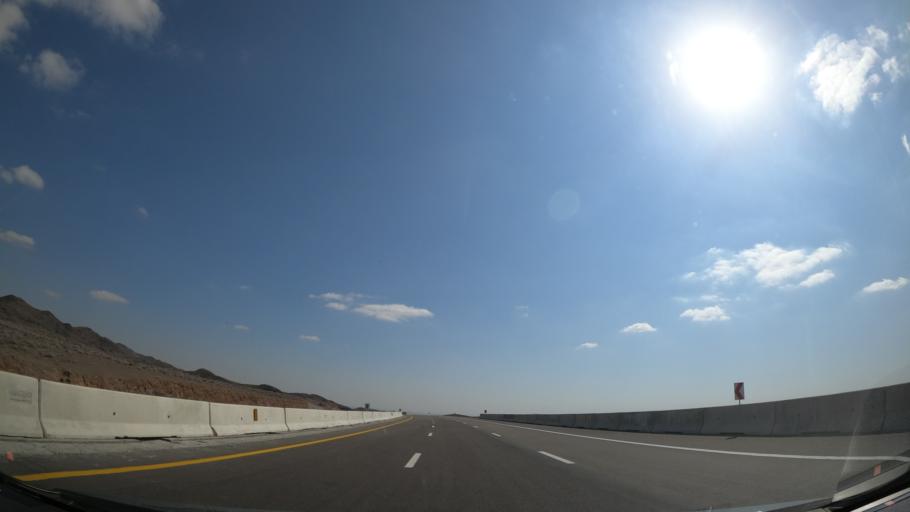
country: IR
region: Alborz
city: Eshtehard
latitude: 35.6668
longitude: 50.6472
